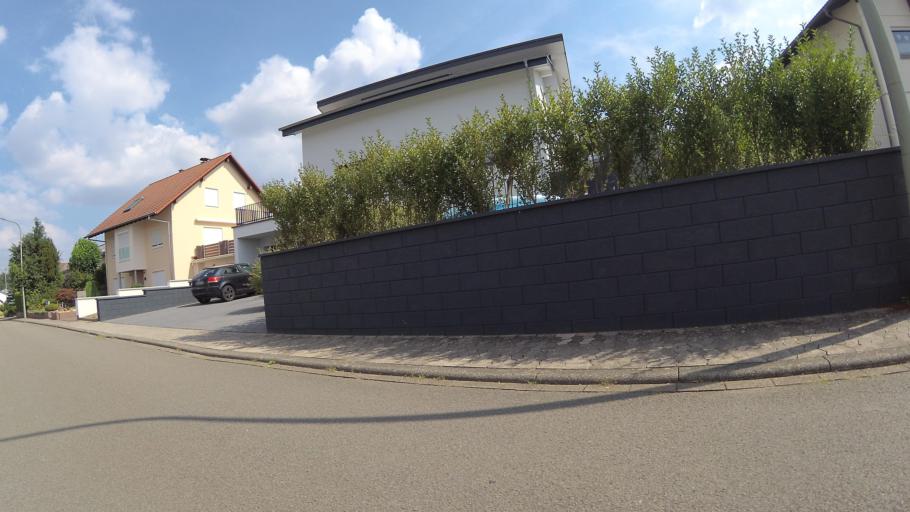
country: DE
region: Rheinland-Pfalz
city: Contwig
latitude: 49.2559
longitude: 7.4254
